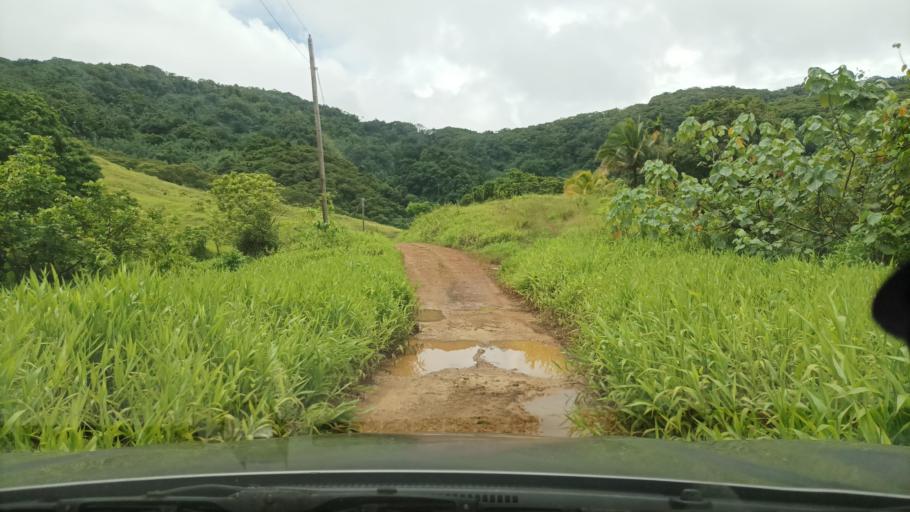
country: FM
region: Pohnpei
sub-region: Madolenihm Municipality
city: Madolenihm Municipality Government
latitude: 6.8939
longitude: 158.2886
